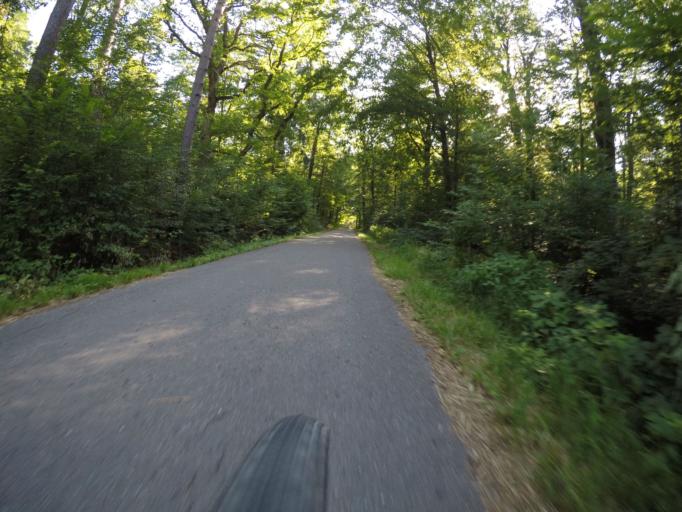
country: DE
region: Baden-Wuerttemberg
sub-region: Regierungsbezirk Stuttgart
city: Gerlingen
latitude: 48.7639
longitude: 9.1117
